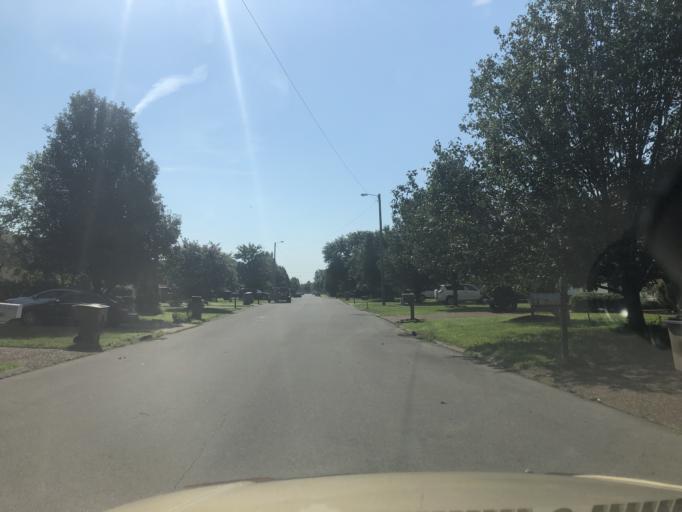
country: US
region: Tennessee
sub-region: Davidson County
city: Lakewood
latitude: 36.2398
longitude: -86.6994
